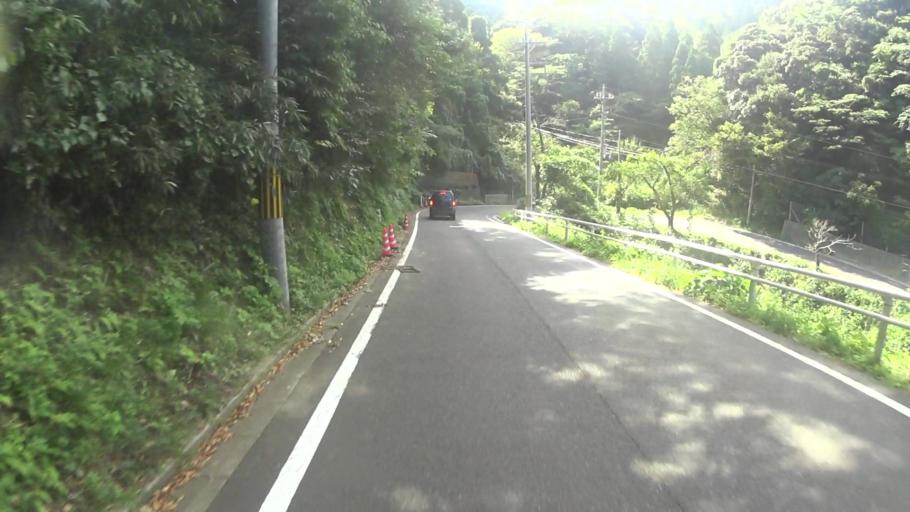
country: JP
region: Kyoto
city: Miyazu
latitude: 35.7485
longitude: 135.2515
